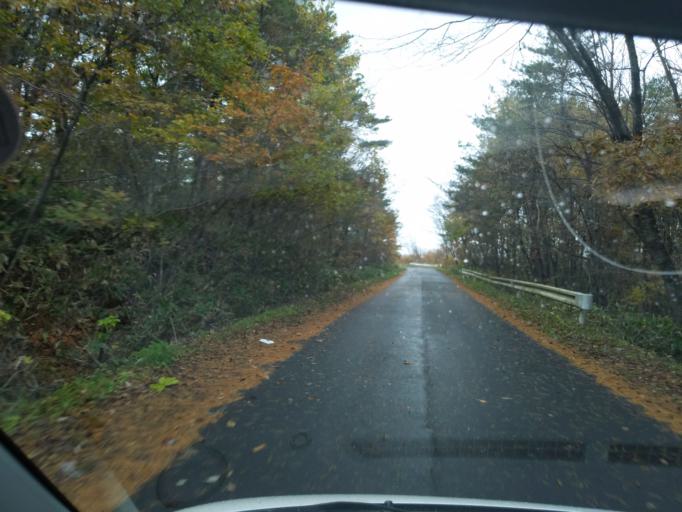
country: JP
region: Iwate
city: Mizusawa
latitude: 39.0780
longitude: 141.0238
